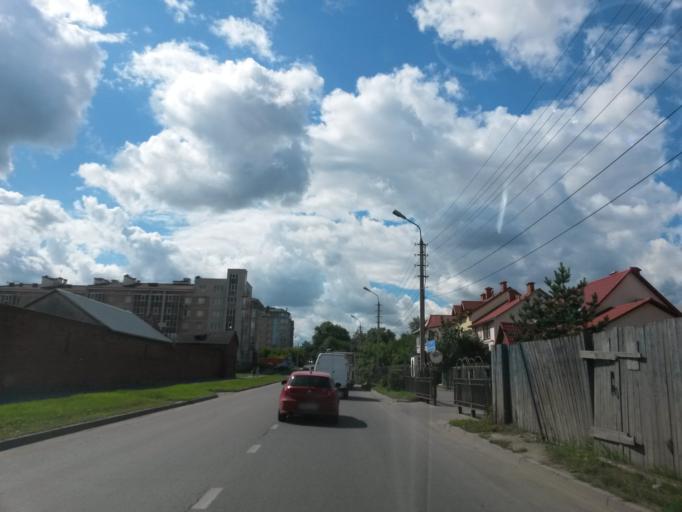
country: RU
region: Jaroslavl
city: Yaroslavl
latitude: 57.6072
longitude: 39.8726
